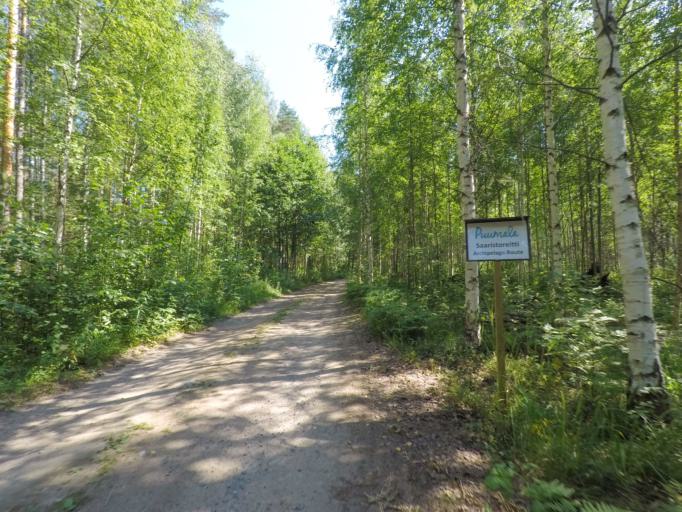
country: FI
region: Southern Savonia
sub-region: Mikkeli
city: Puumala
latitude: 61.4306
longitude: 28.0034
